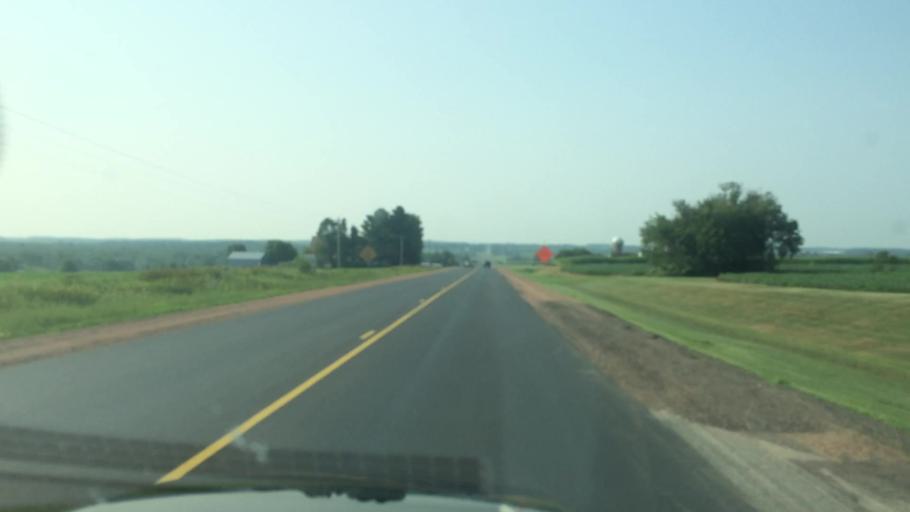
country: US
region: Wisconsin
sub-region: Marathon County
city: Stratford
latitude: 44.8359
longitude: -90.0792
